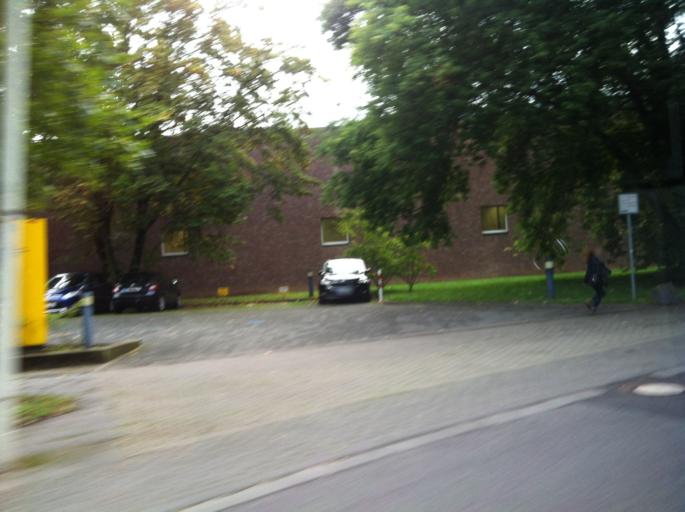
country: DE
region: North Rhine-Westphalia
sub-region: Regierungsbezirk Koln
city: Bonn
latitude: 50.7139
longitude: 7.1319
